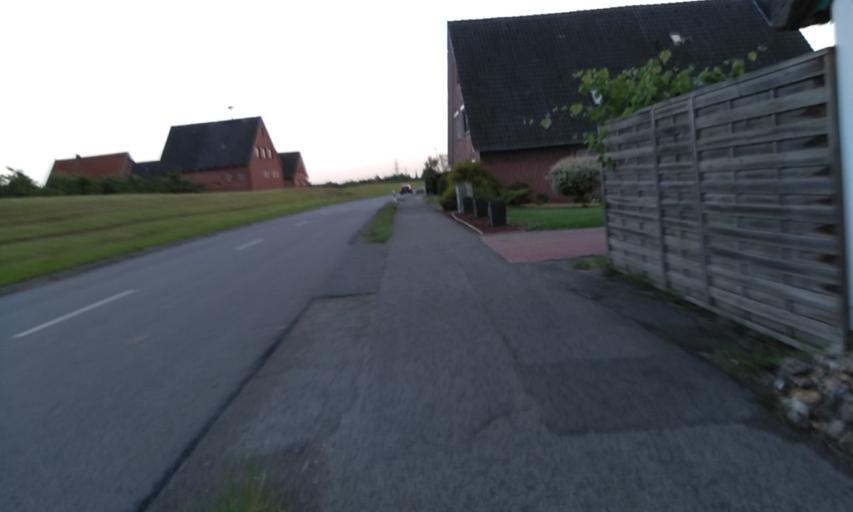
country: DE
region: Lower Saxony
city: Buxtehude
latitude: 53.5015
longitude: 9.7257
